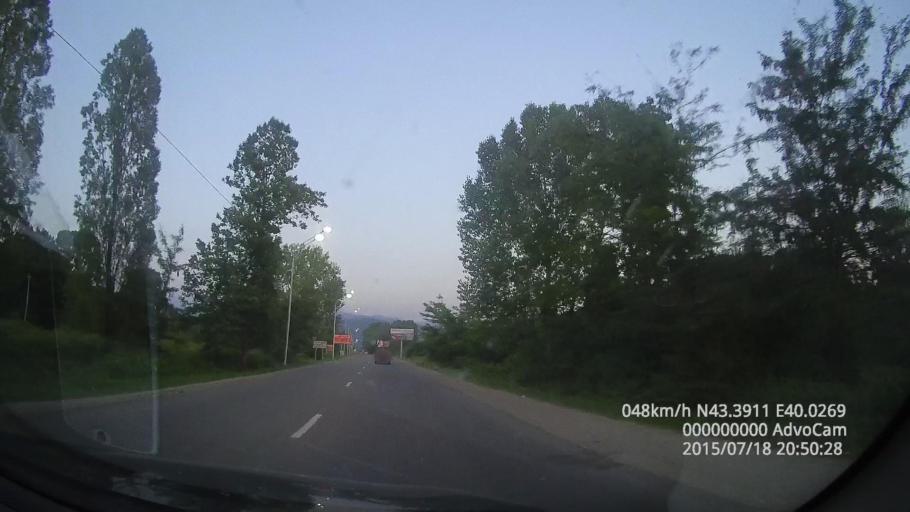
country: GE
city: Gantiadi
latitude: 43.3910
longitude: 40.0281
